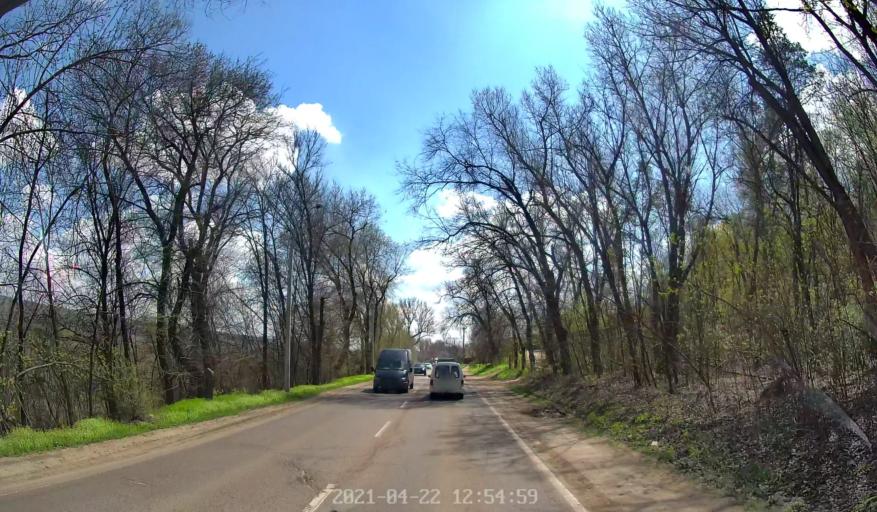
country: MD
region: Chisinau
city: Chisinau
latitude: 46.9665
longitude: 28.9161
